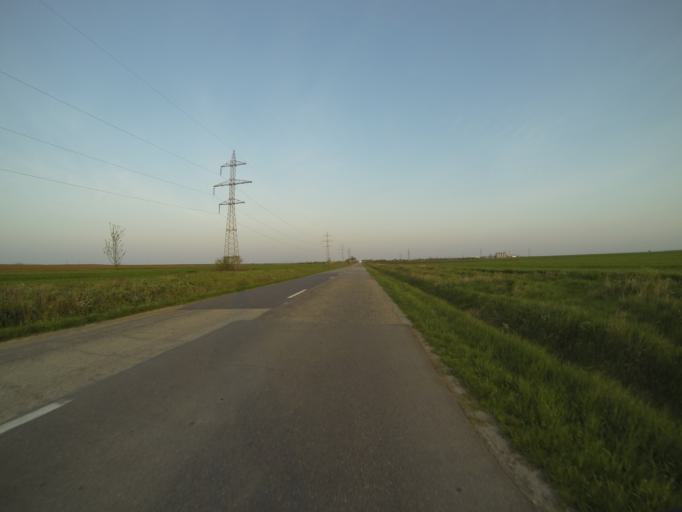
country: RO
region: Dolj
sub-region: Comuna Dranicu
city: Dranic
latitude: 44.0622
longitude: 23.8214
